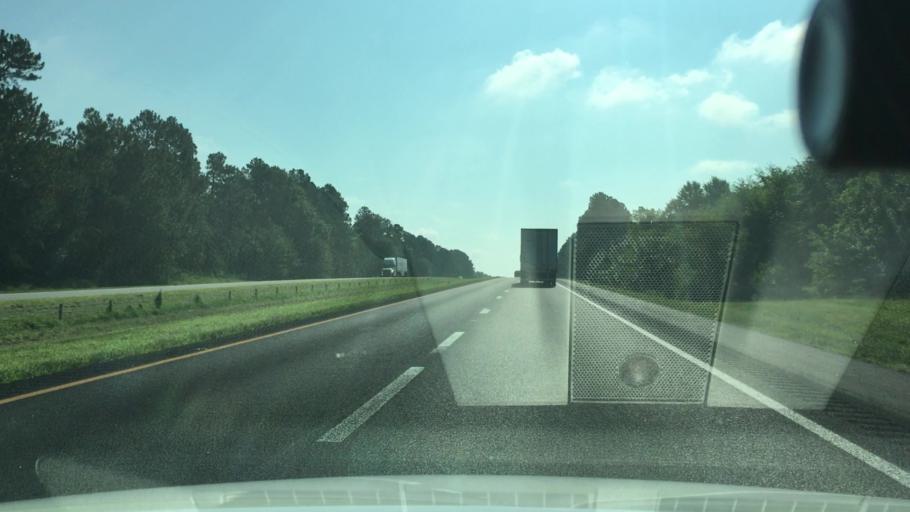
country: US
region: South Carolina
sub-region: Aiken County
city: Graniteville
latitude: 33.6347
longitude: -81.7693
